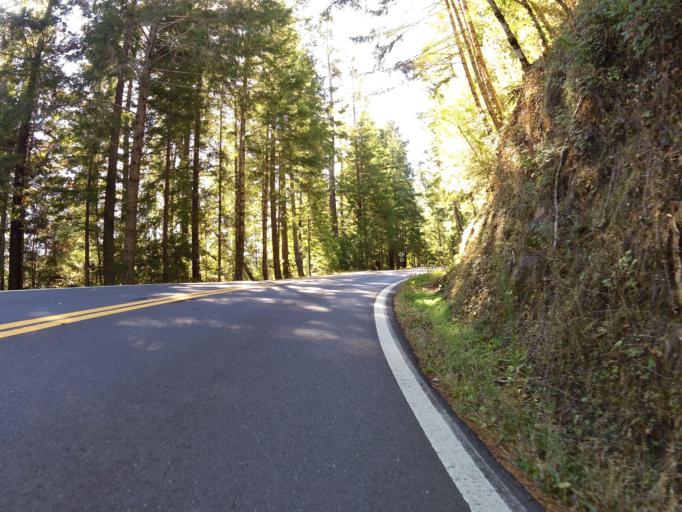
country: US
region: California
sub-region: Humboldt County
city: Redway
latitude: 39.8548
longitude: -123.7297
